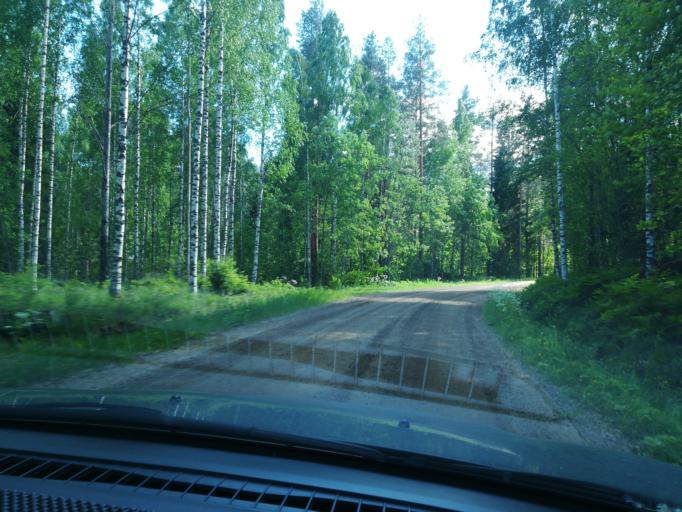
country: FI
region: Southern Savonia
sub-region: Mikkeli
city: Puumala
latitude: 61.6627
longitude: 28.1420
